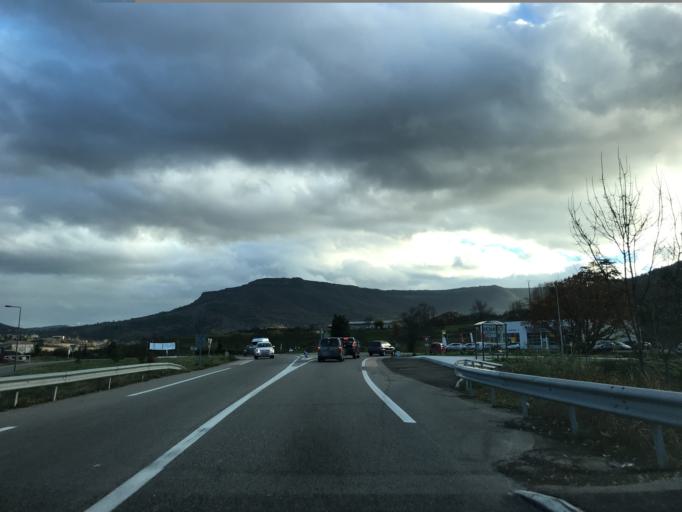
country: FR
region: Rhone-Alpes
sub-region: Departement de l'Ardeche
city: Alissas
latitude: 44.7108
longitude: 4.6390
